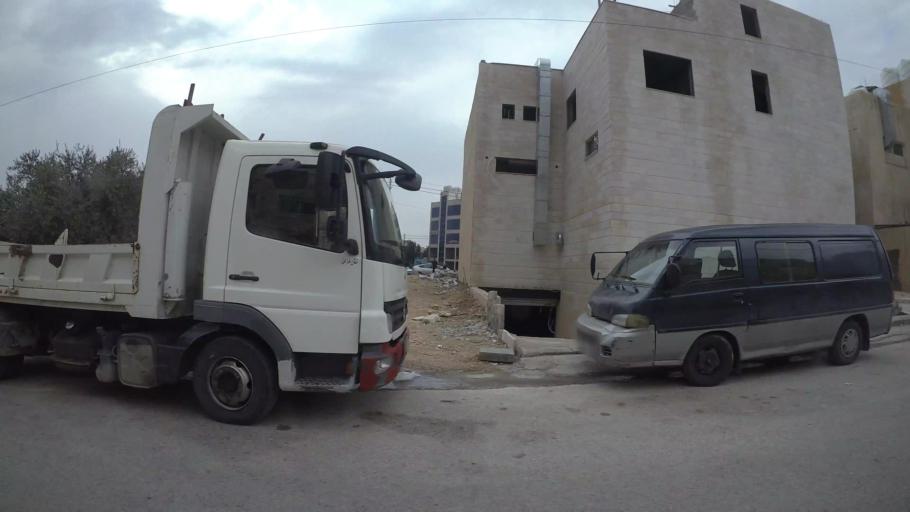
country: JO
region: Amman
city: Umm as Summaq
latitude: 31.8873
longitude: 35.8577
